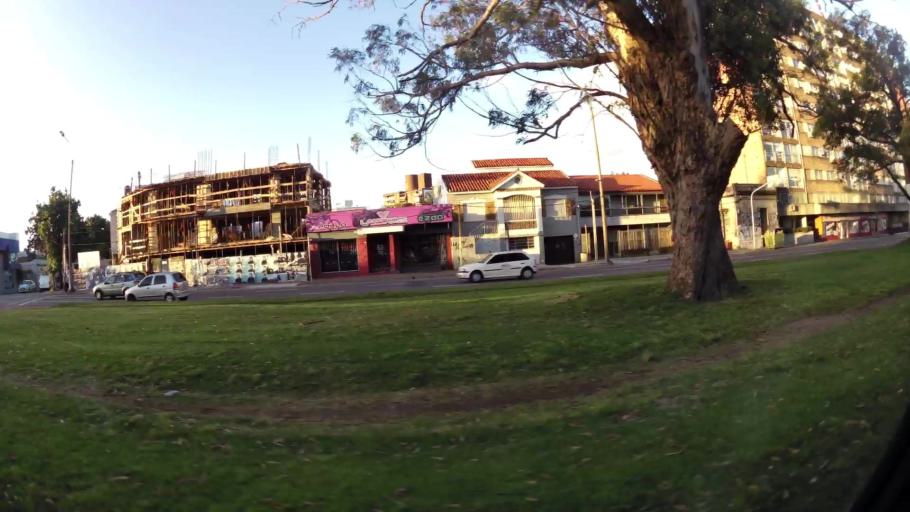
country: UY
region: Montevideo
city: Montevideo
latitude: -34.8871
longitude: -56.1396
